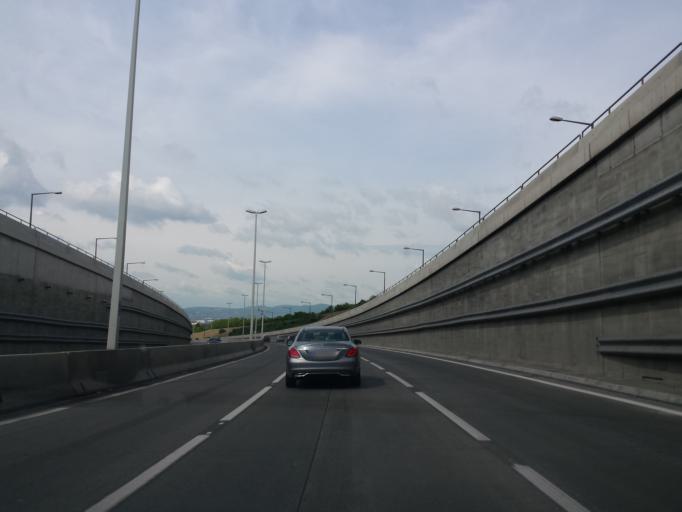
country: AT
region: Lower Austria
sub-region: Politischer Bezirk Wien-Umgebung
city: Leopoldsdorf
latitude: 48.1600
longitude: 16.3800
